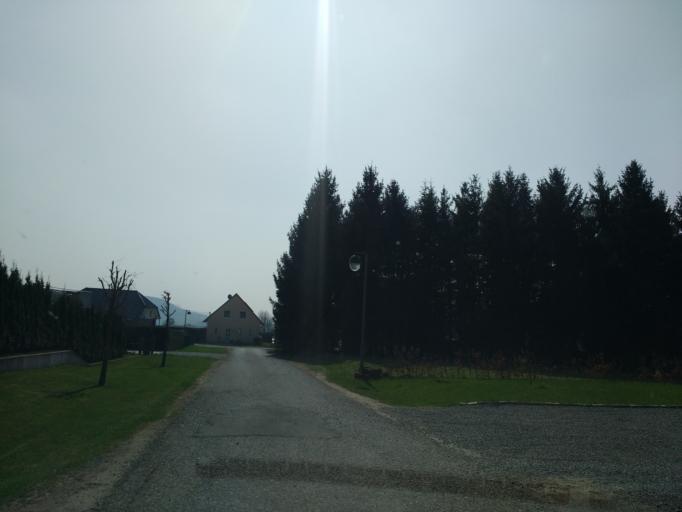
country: DE
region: North Rhine-Westphalia
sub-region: Regierungsbezirk Detmold
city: Lugde
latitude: 51.9767
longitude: 9.1862
